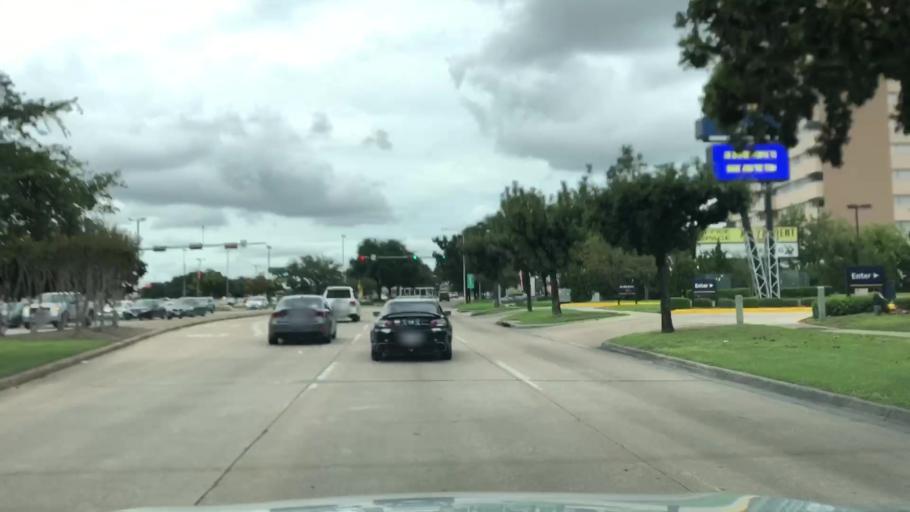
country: US
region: Texas
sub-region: Harris County
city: Piney Point Village
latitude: 29.7051
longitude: -95.5179
